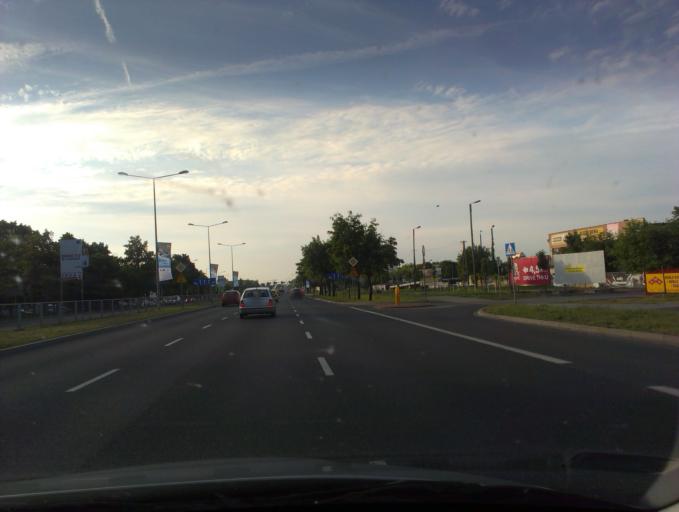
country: PL
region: Greater Poland Voivodeship
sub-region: Leszno
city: Leszno
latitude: 51.8393
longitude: 16.5947
